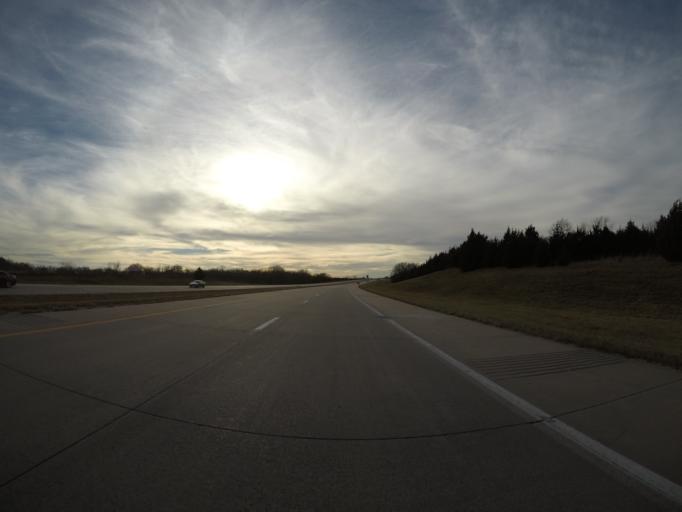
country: US
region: Kansas
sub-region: Franklin County
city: Ottawa
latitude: 38.5322
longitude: -95.3840
